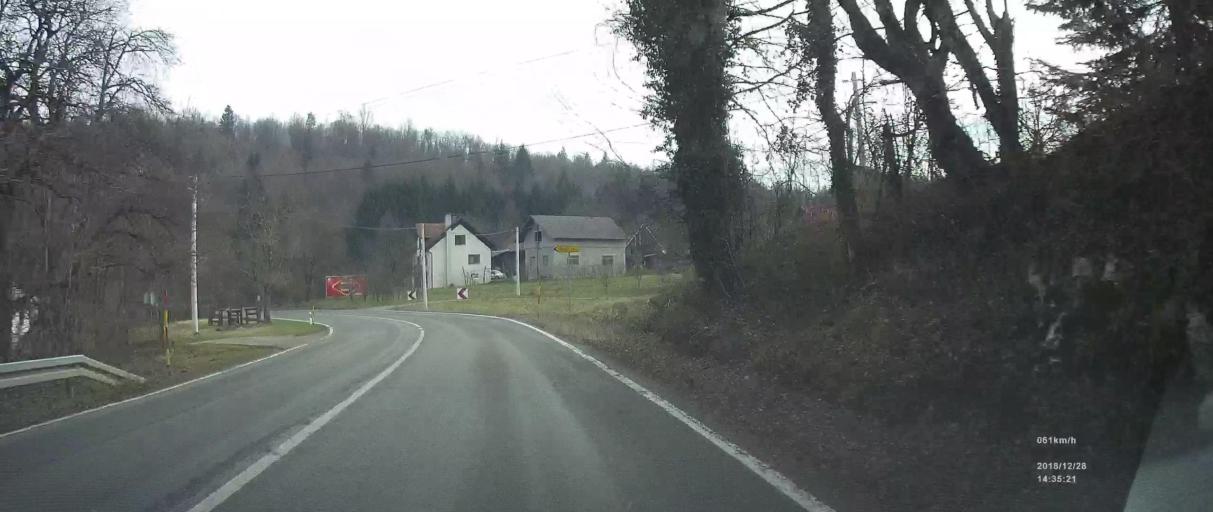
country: HR
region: Primorsko-Goranska
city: Vrbovsko
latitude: 45.4210
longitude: 15.1833
